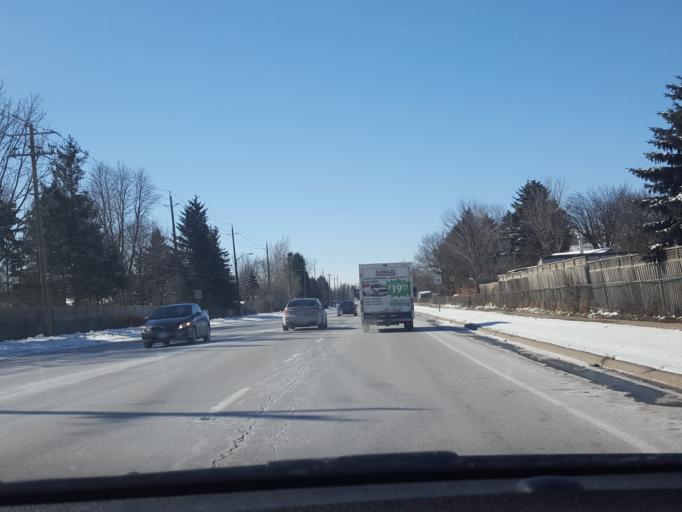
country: CA
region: Ontario
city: Waterloo
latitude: 43.4931
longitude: -80.5575
